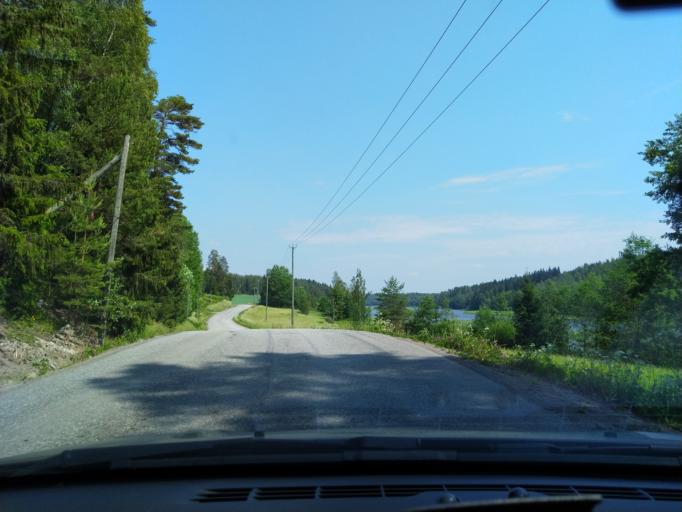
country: FI
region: Uusimaa
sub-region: Helsinki
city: Lohja
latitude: 60.3448
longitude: 24.0865
